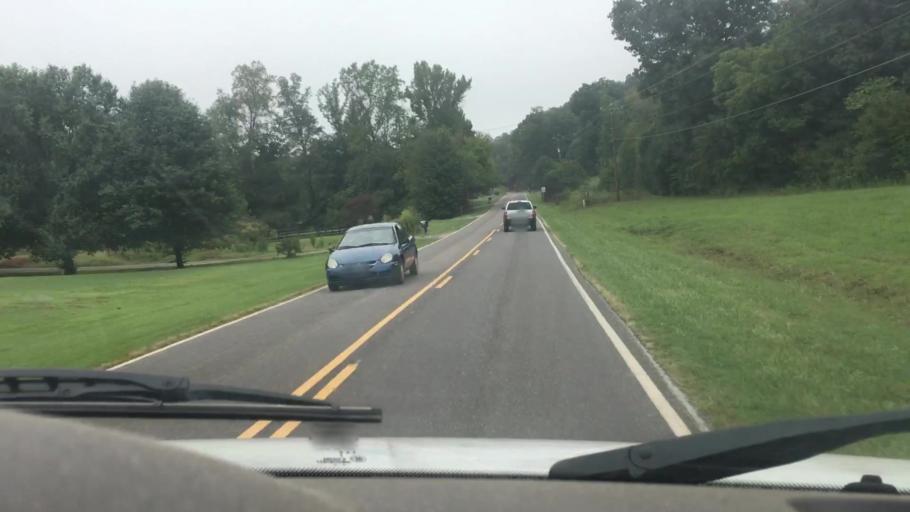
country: US
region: North Carolina
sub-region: Gaston County
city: Davidson
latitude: 35.5210
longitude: -80.7748
